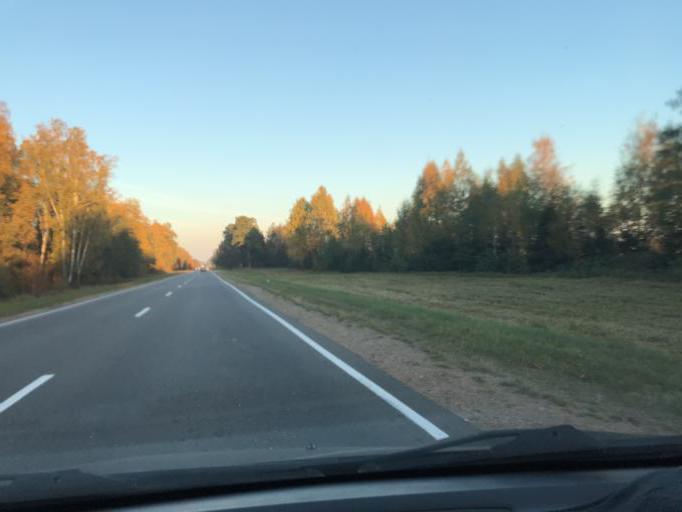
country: BY
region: Minsk
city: Staryya Darohi
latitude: 53.0615
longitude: 28.4960
